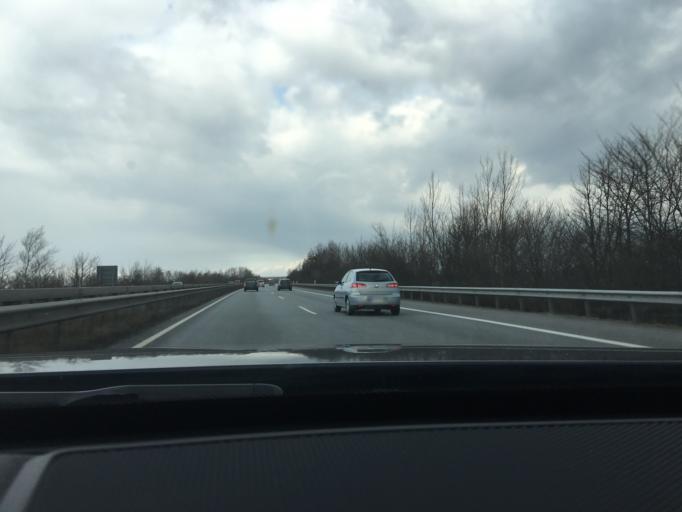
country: DE
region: Lower Saxony
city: Driftsethe
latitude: 53.3832
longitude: 8.5748
